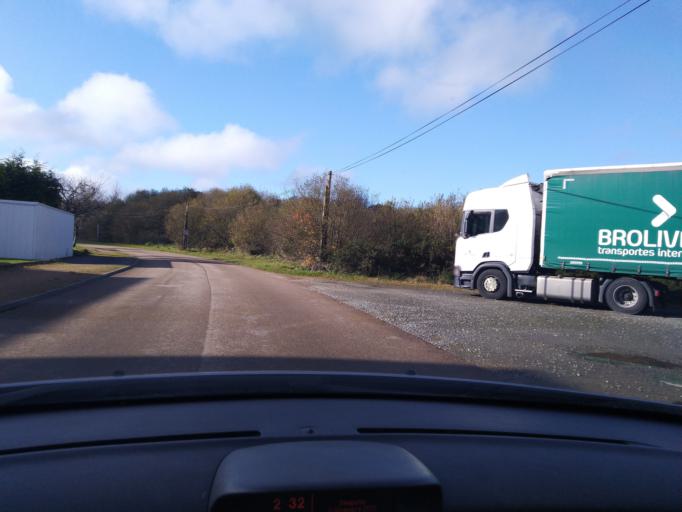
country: FR
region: Brittany
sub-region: Departement du Finistere
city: Guerlesquin
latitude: 48.5126
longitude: -3.5861
